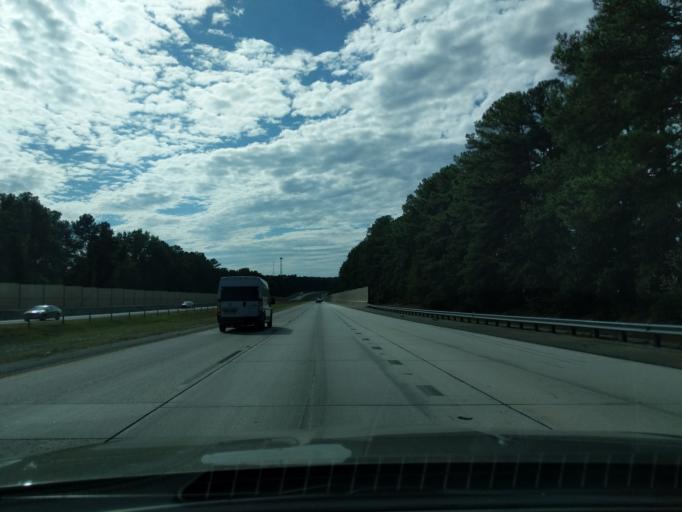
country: US
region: Georgia
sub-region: Columbia County
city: Evans
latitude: 33.4811
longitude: -82.1379
